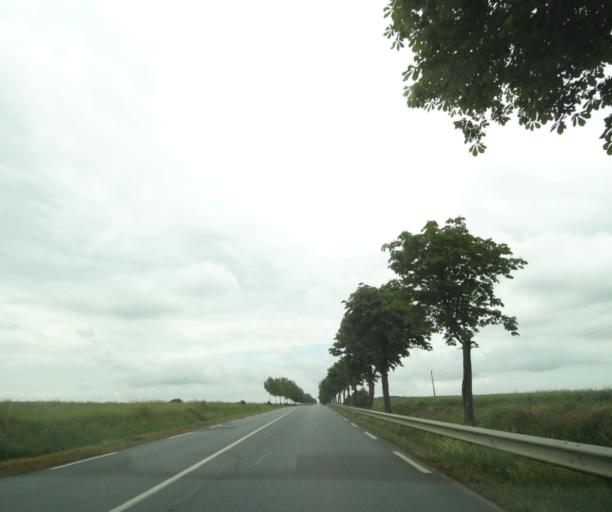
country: FR
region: Poitou-Charentes
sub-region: Departement des Deux-Sevres
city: Saint-Jean-de-Thouars
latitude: 46.9305
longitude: -0.1997
